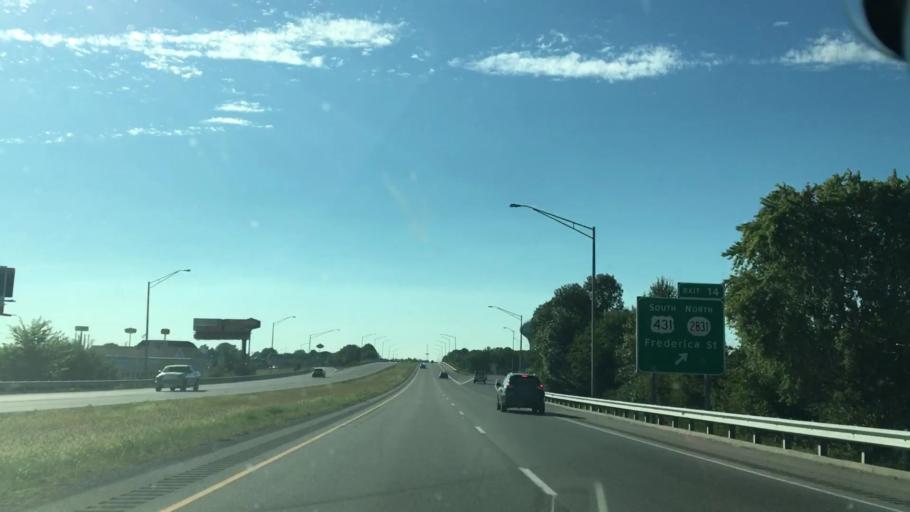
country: US
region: Kentucky
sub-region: Daviess County
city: Owensboro
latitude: 37.7277
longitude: -87.1169
